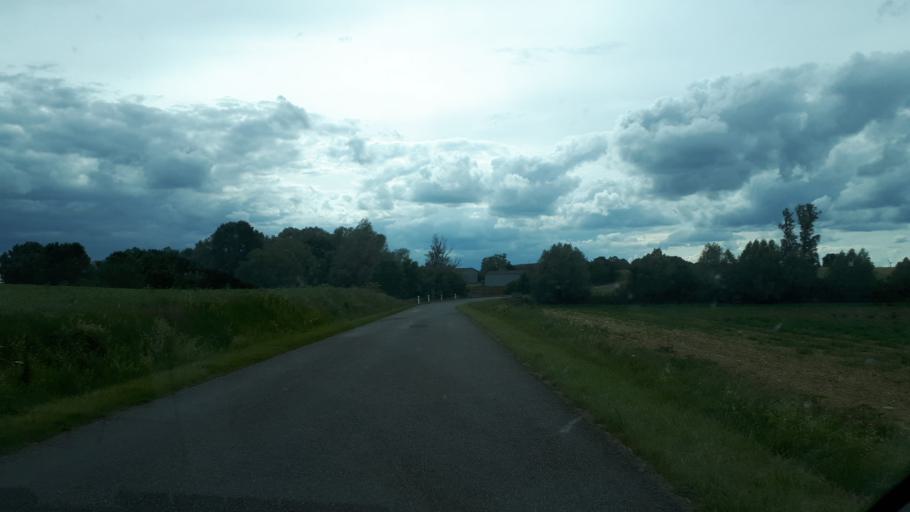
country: FR
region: Centre
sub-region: Departement de l'Indre
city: Reuilly
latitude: 47.0947
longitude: 1.9958
